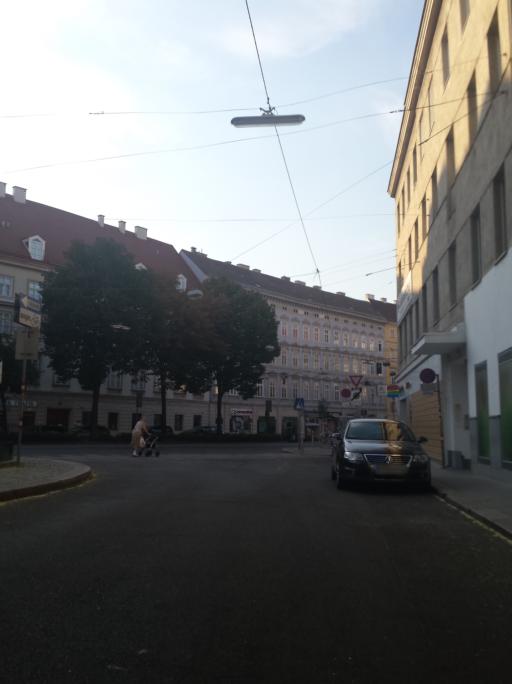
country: AT
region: Vienna
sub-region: Wien Stadt
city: Vienna
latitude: 48.1918
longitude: 16.3672
